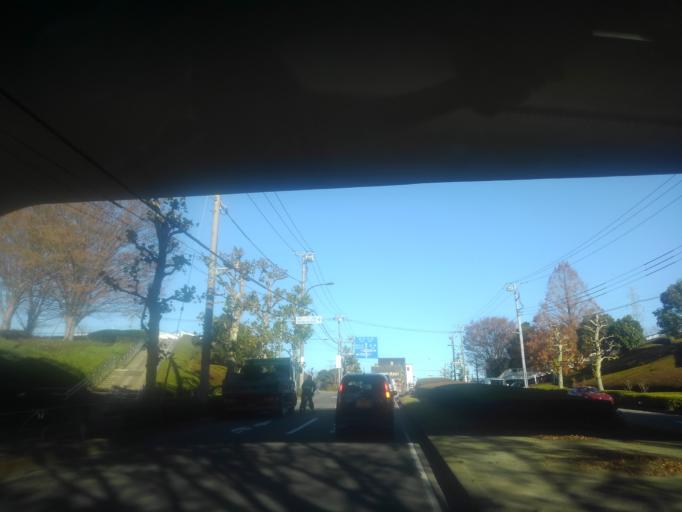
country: JP
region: Tokyo
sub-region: Machida-shi
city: Machida
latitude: 35.6098
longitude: 139.4431
